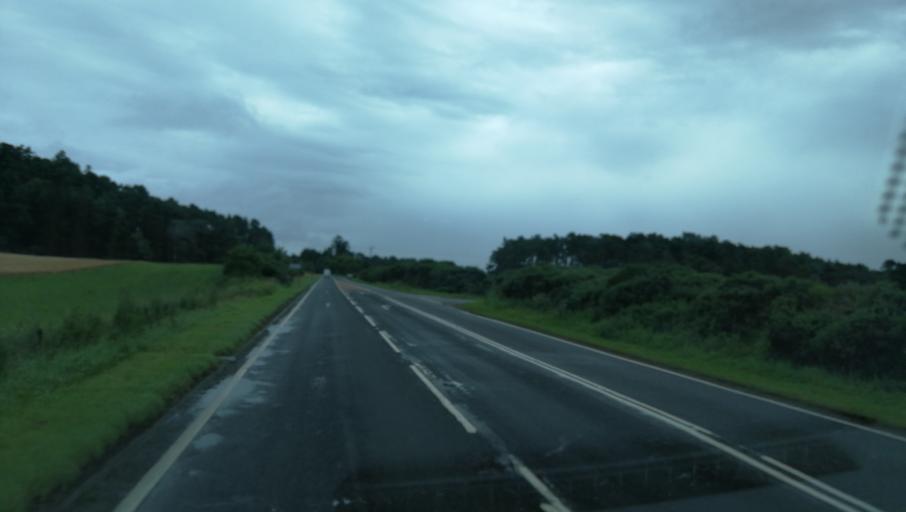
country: GB
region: Scotland
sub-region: Highland
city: Inverness
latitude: 57.4507
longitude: -4.2824
